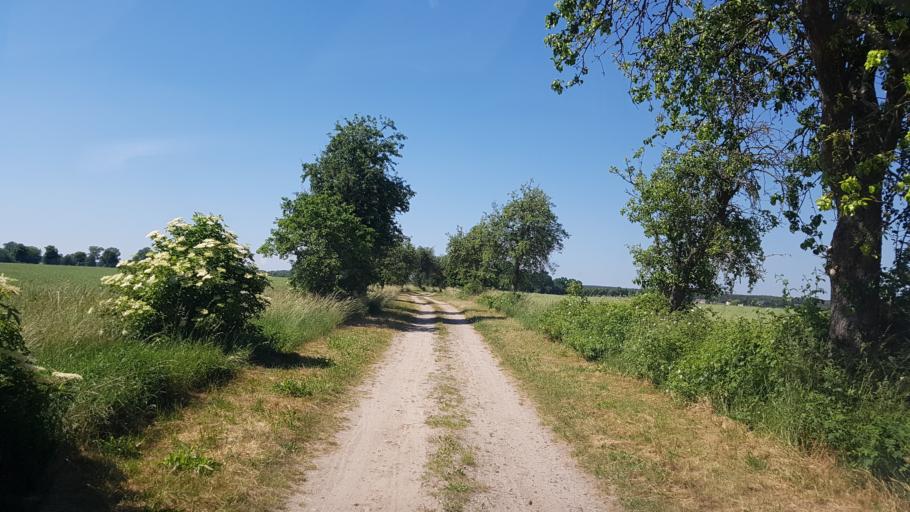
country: DE
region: Brandenburg
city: Sonnewalde
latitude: 51.6998
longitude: 13.6685
